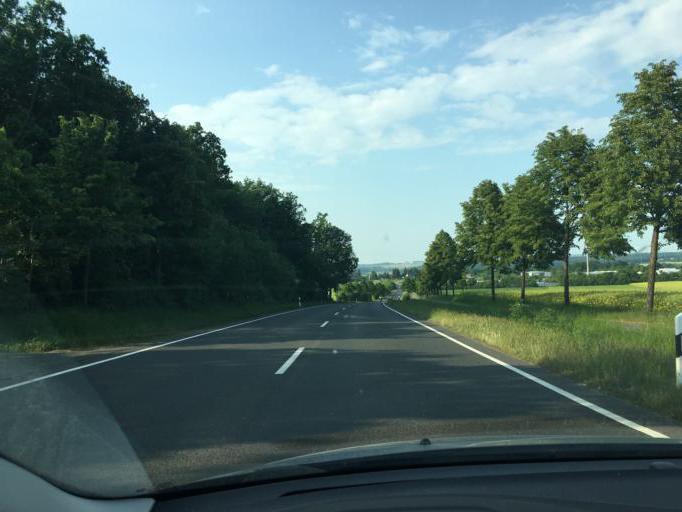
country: DE
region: Saxony
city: Grossbothen
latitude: 51.1733
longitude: 12.7595
